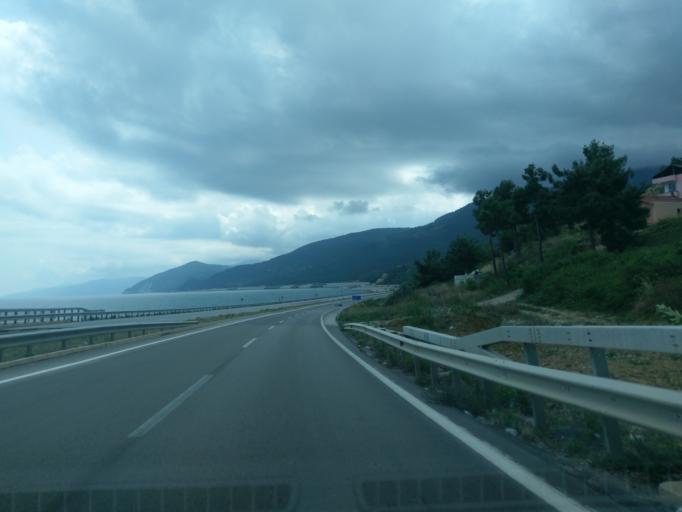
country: TR
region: Sinop
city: Gerze
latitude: 41.7821
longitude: 35.2010
